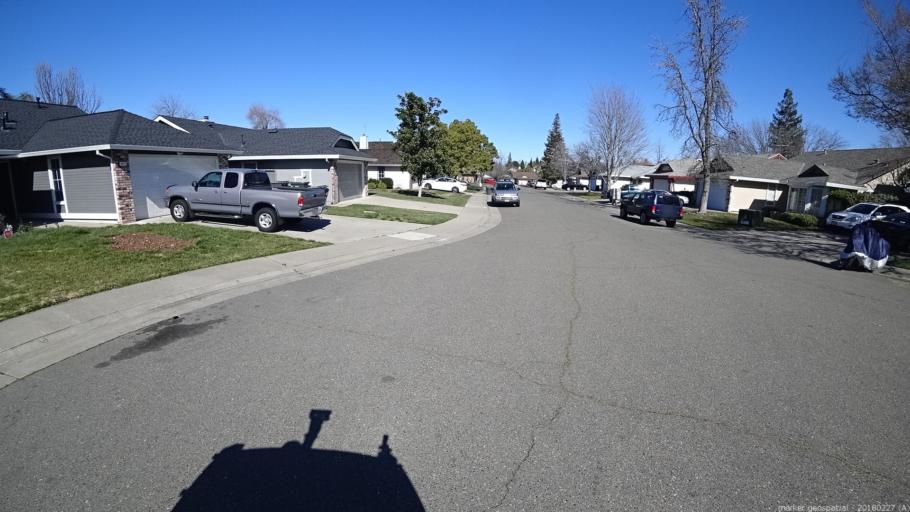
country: US
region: California
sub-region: Sacramento County
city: Antelope
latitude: 38.7167
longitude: -121.3490
